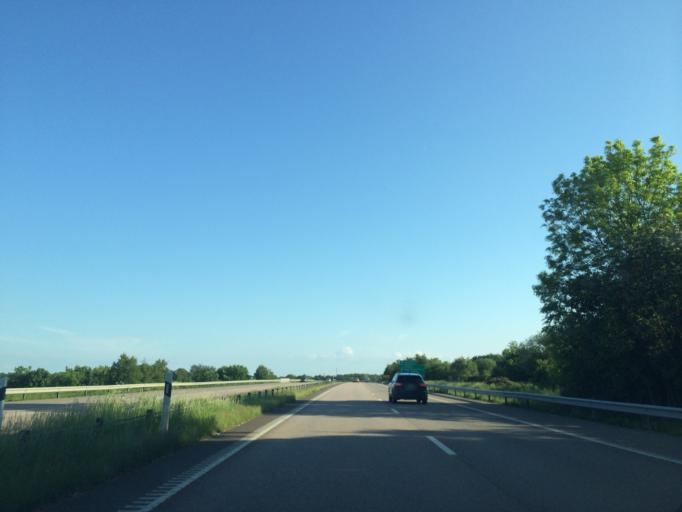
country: SE
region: Skane
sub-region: Helsingborg
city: Barslov
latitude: 56.0315
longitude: 12.7857
